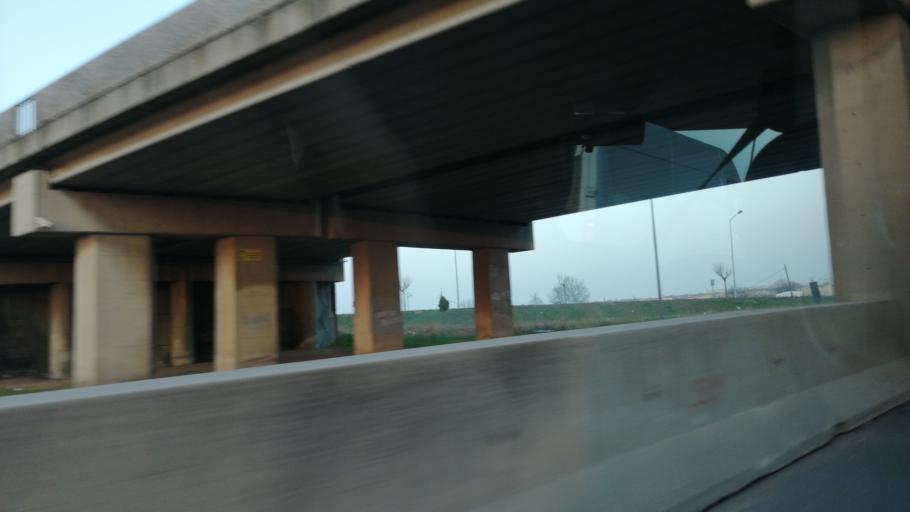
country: TR
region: Yalova
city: Taskopru
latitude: 40.6874
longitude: 29.4322
